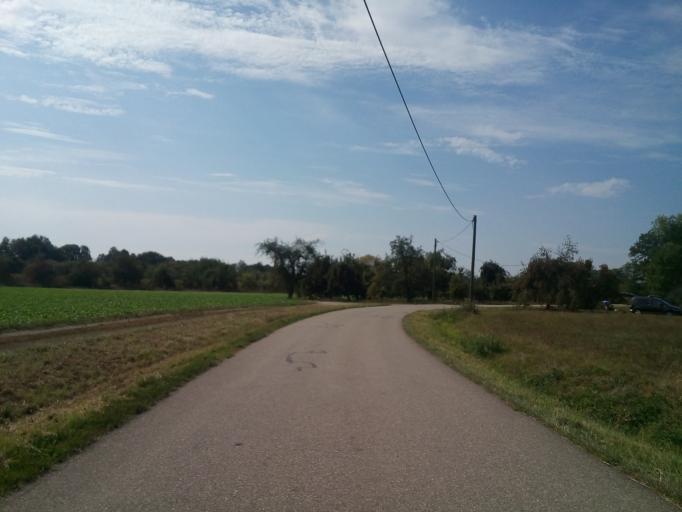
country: DE
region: Baden-Wuerttemberg
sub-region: Karlsruhe Region
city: Ottersweier
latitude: 48.6693
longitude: 8.0940
